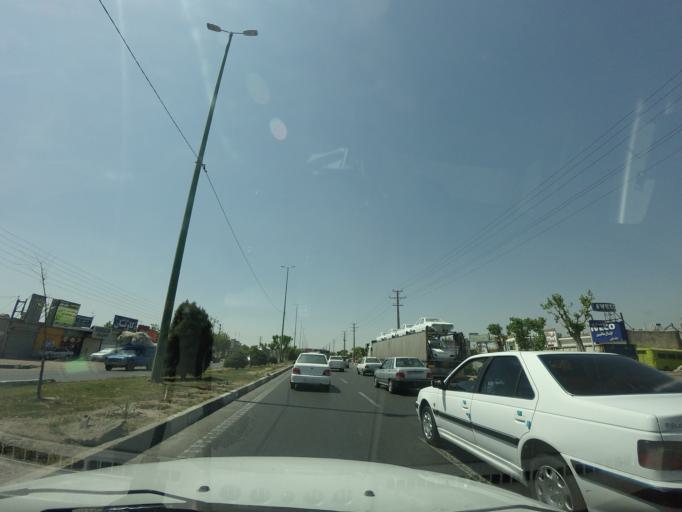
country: IR
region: Tehran
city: Eslamshahr
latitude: 35.5861
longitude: 51.2816
